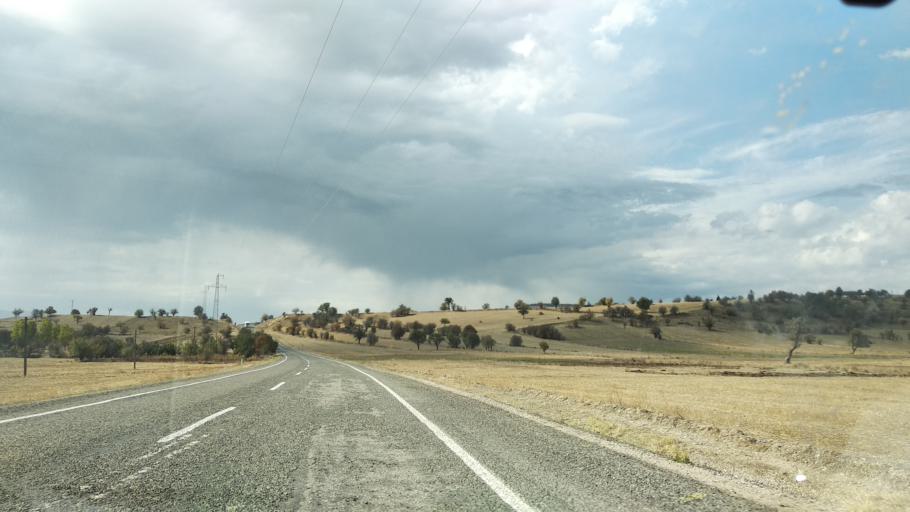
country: TR
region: Bolu
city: Seben
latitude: 40.3761
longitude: 31.5166
